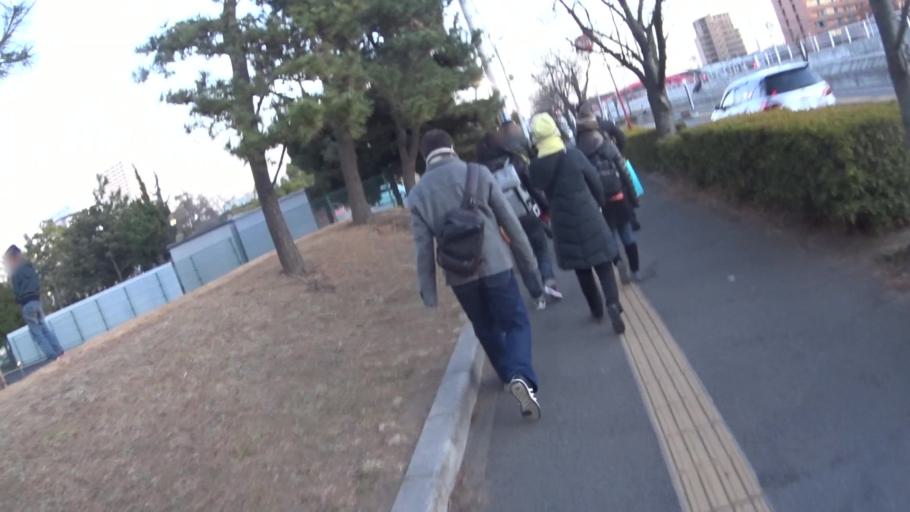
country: JP
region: Tokyo
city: Urayasu
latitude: 35.6475
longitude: 139.9067
